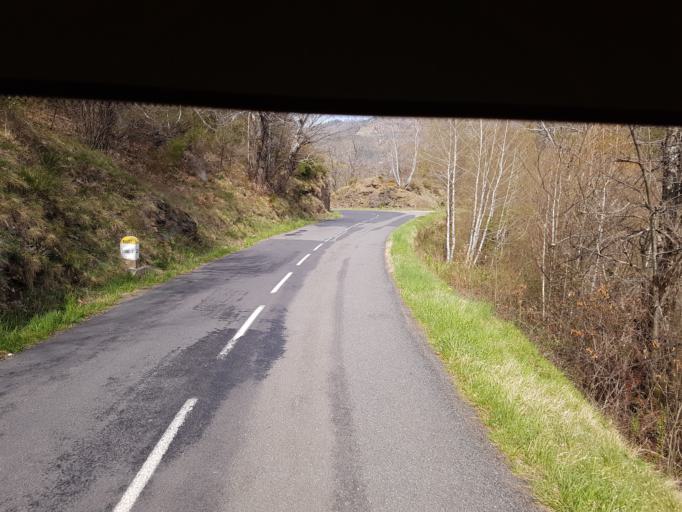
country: FR
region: Languedoc-Roussillon
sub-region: Departement de la Lozere
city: Florac
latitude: 44.2802
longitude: 3.5874
